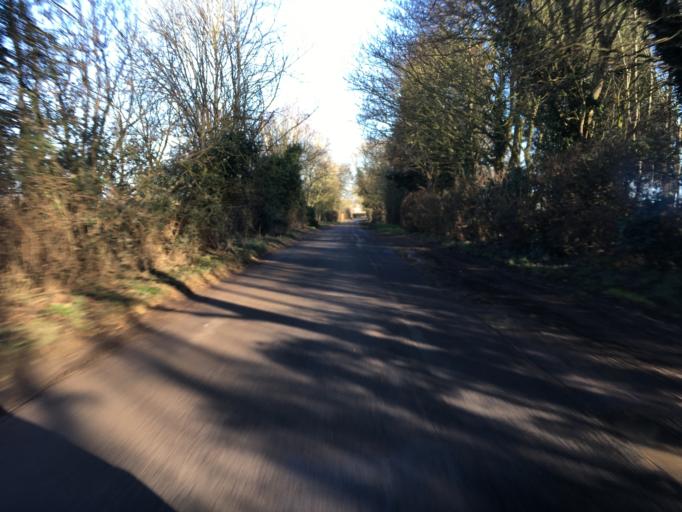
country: GB
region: England
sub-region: Warwickshire
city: Stratford-upon-Avon
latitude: 52.1941
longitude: -1.6655
